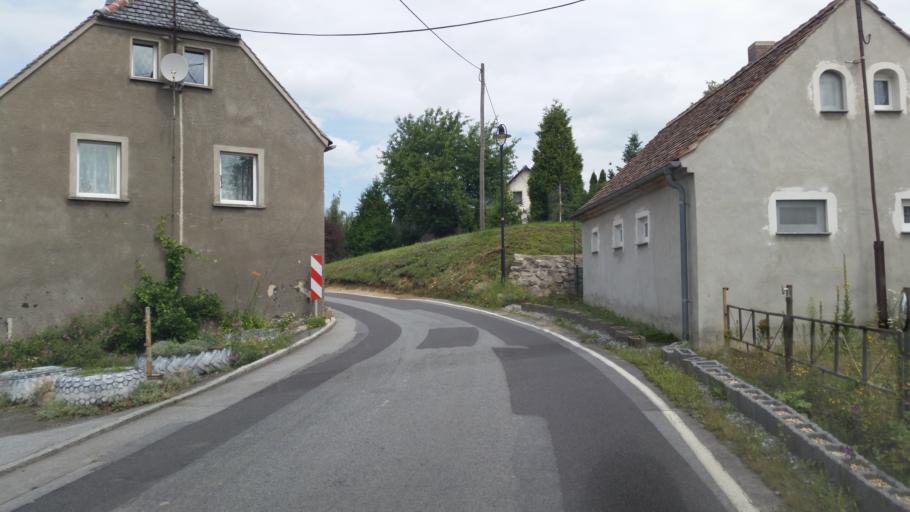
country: DE
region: Saxony
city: Puschwitz
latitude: 51.2214
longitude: 14.3148
